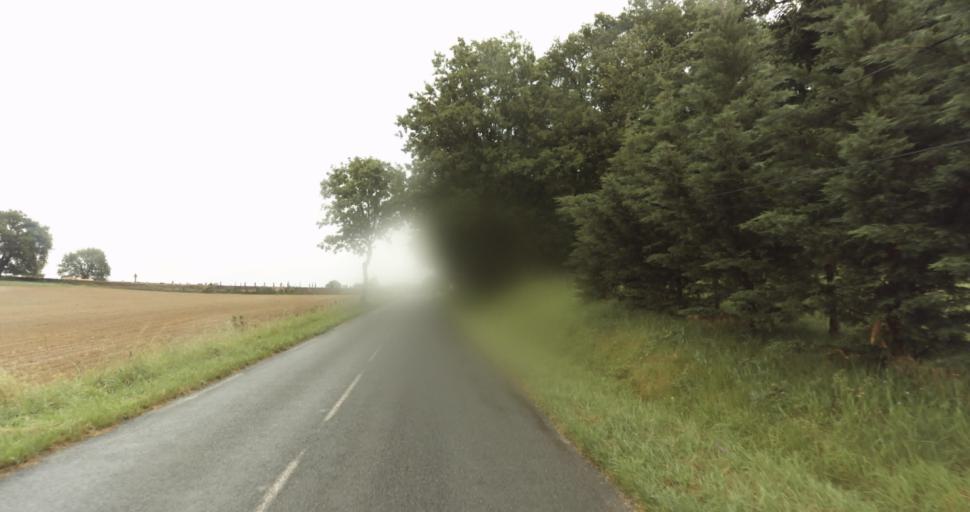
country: FR
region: Aquitaine
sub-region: Departement de la Dordogne
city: Beaumont-du-Perigord
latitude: 44.7793
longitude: 0.8236
